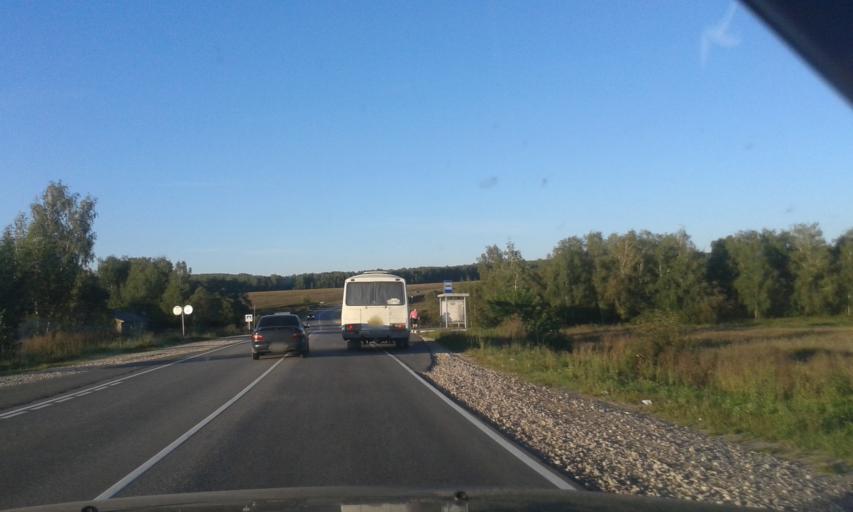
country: RU
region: Tula
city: Krapivna
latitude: 54.1159
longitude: 37.2219
